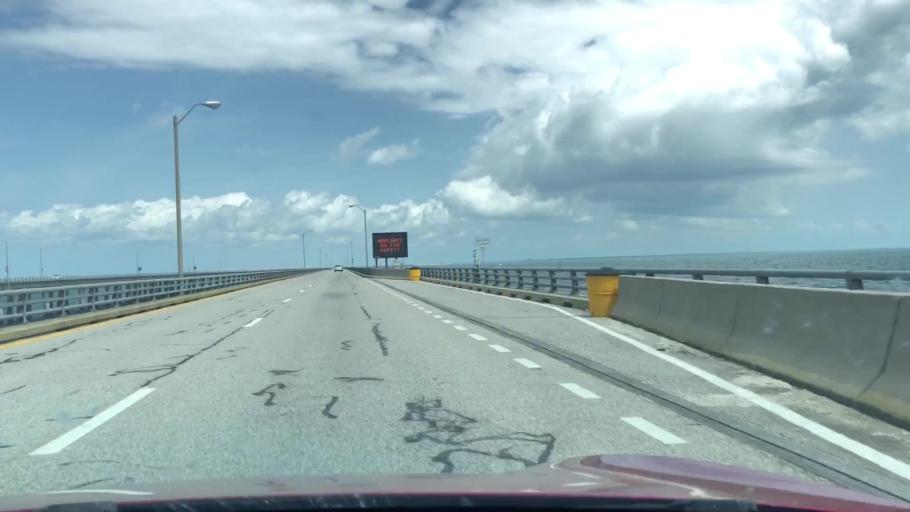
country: US
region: Virginia
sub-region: City of Virginia Beach
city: Virginia Beach
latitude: 36.9956
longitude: -76.1004
